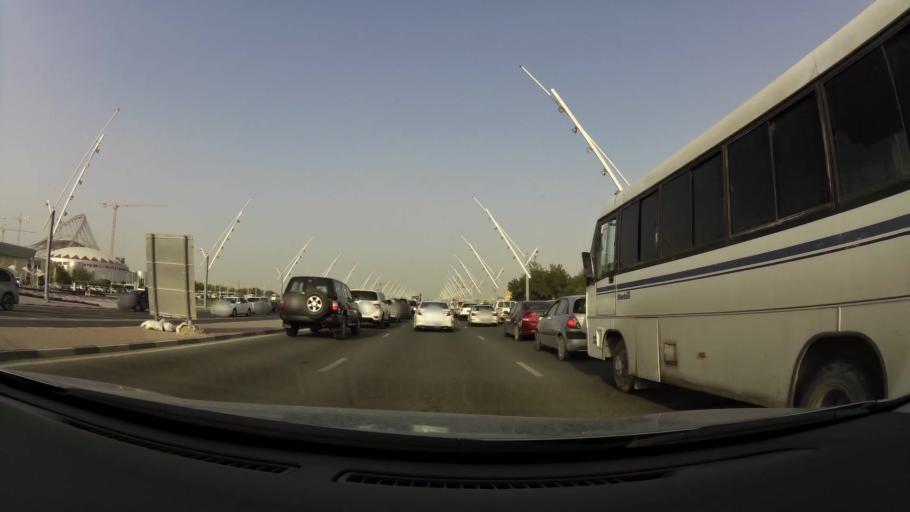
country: QA
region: Baladiyat ar Rayyan
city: Ar Rayyan
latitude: 25.2582
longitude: 51.4471
